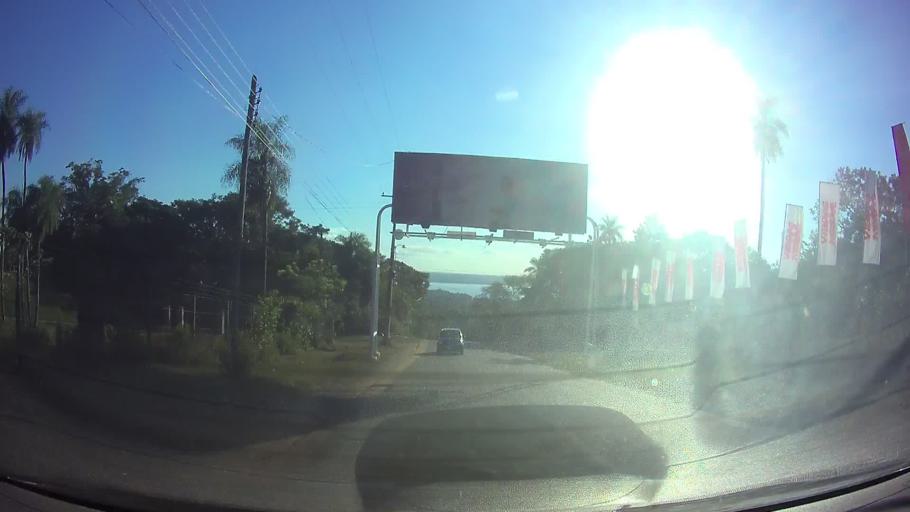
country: PY
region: Cordillera
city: San Bernardino
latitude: -25.3164
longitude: -57.2673
